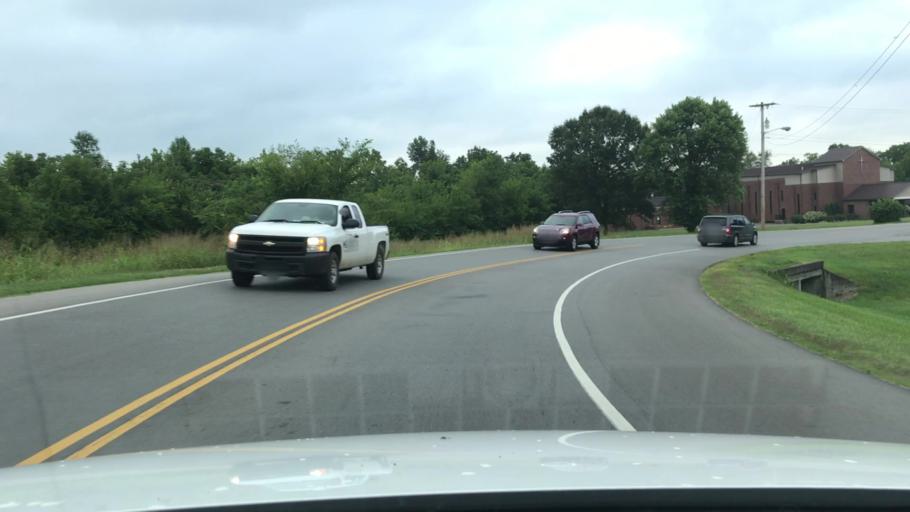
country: US
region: Tennessee
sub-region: Sumner County
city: Gallatin
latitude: 36.3772
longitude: -86.4686
